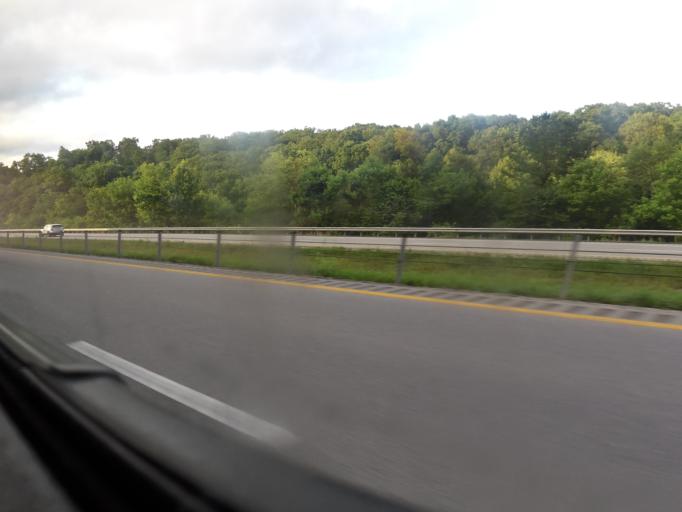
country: US
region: Kentucky
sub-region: Rockcastle County
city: Mount Vernon
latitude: 37.3176
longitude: -84.2932
